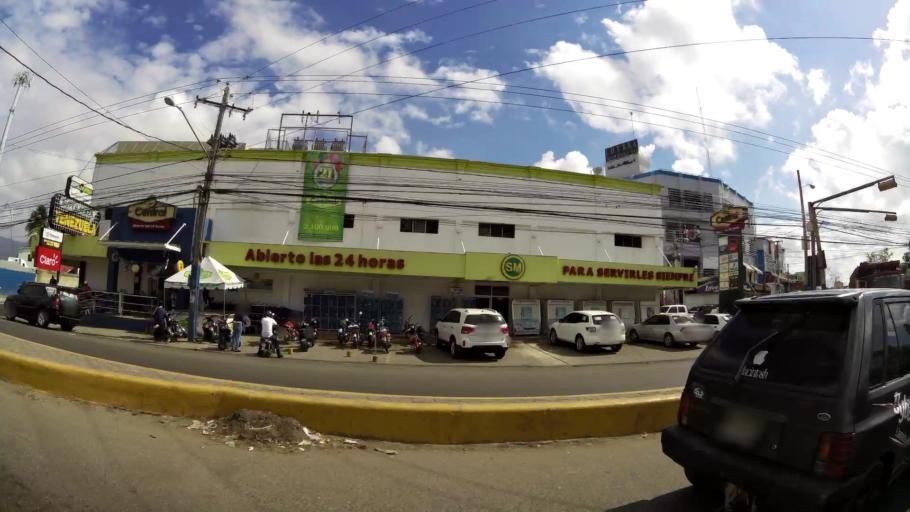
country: DO
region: Santiago
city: Santiago de los Caballeros
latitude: 19.4856
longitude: -70.7120
